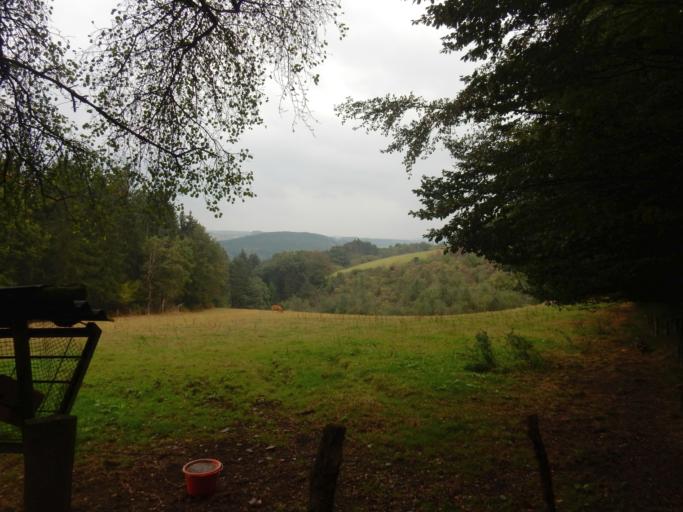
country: LU
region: Diekirch
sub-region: Canton de Wiltz
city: Winseler
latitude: 49.9537
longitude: 5.8996
